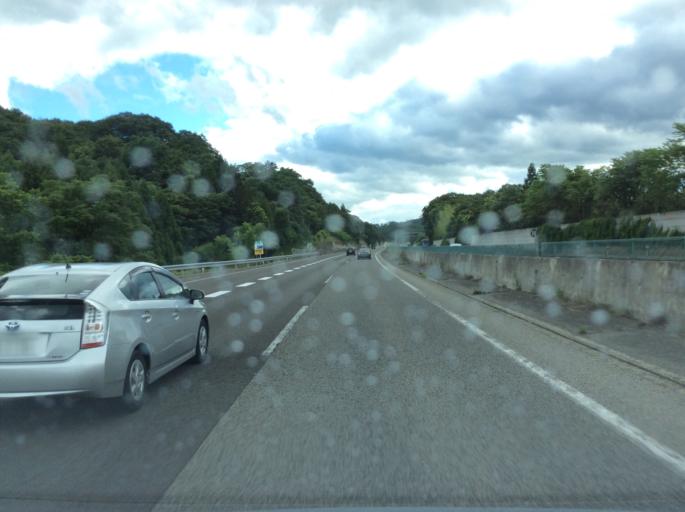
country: JP
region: Fukushima
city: Fukushima-shi
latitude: 37.7019
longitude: 140.4503
